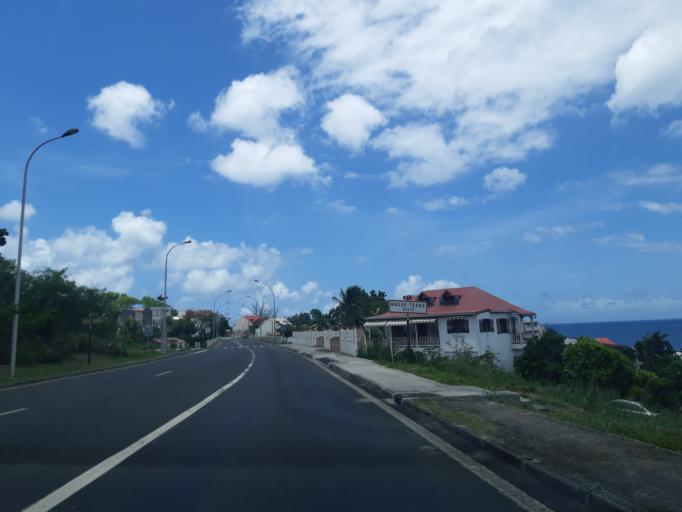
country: GP
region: Guadeloupe
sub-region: Guadeloupe
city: Basse-Terre
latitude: 15.9971
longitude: -61.7271
